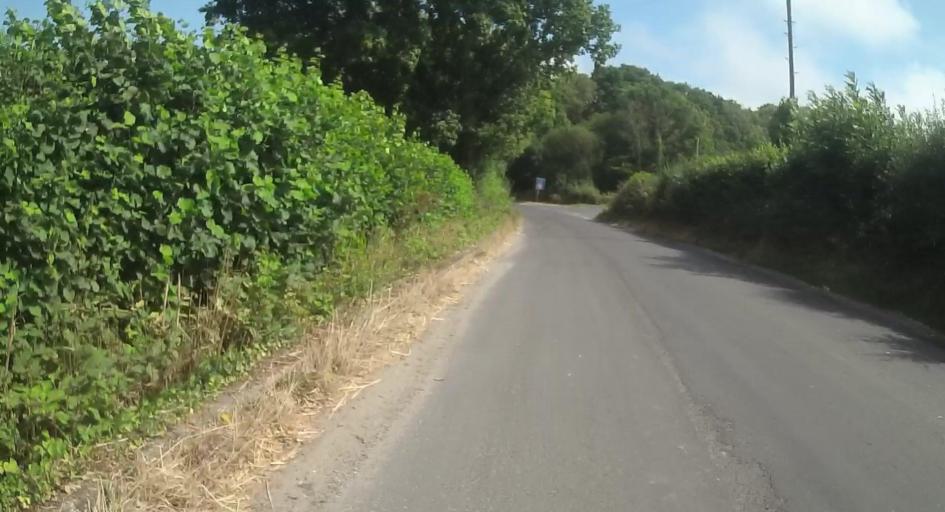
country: GB
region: England
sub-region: Dorset
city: Bovington Camp
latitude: 50.6915
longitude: -2.2692
